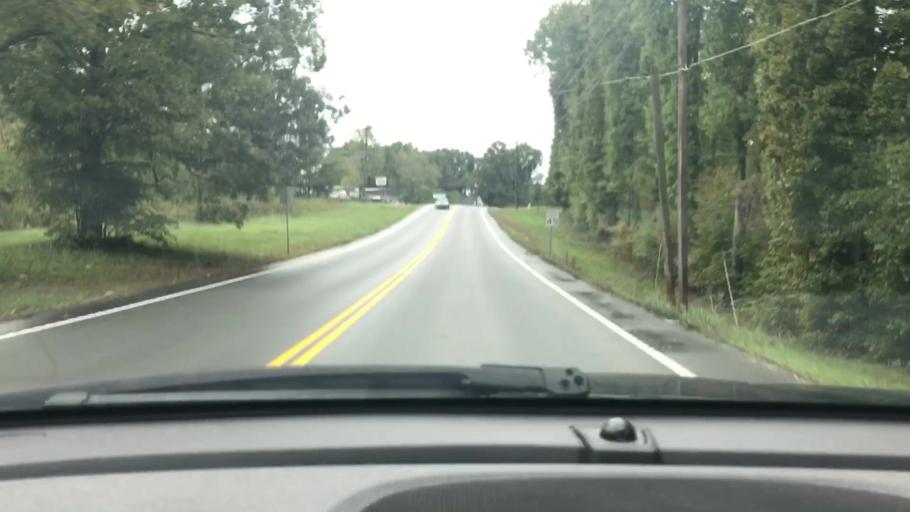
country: US
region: Tennessee
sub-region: Cheatham County
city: Kingston Springs
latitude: 36.1122
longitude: -87.1594
